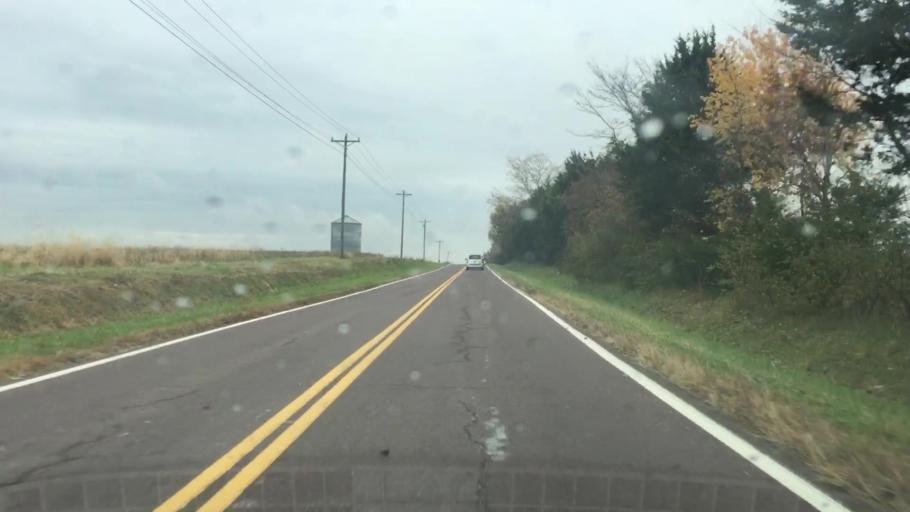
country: US
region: Missouri
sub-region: Callaway County
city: Fulton
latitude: 38.7879
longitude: -91.7852
